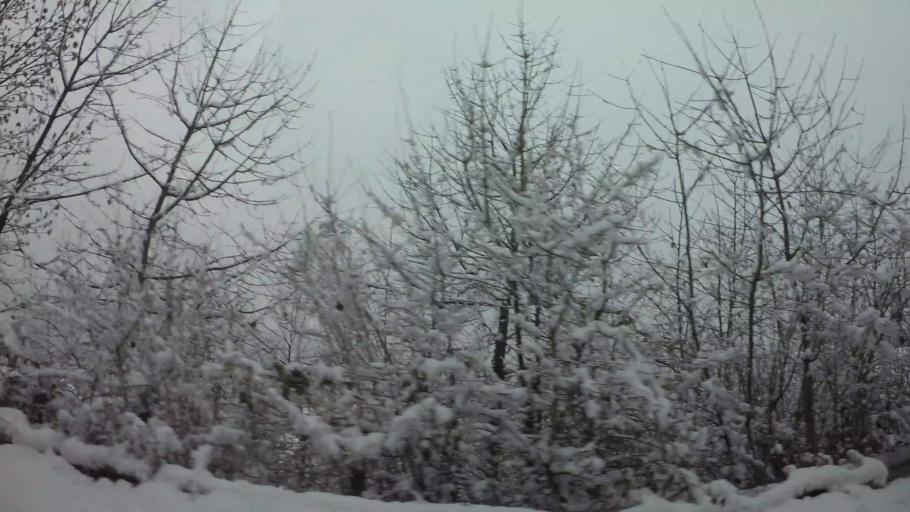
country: BA
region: Federation of Bosnia and Herzegovina
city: Kobilja Glava
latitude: 43.8478
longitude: 18.4118
